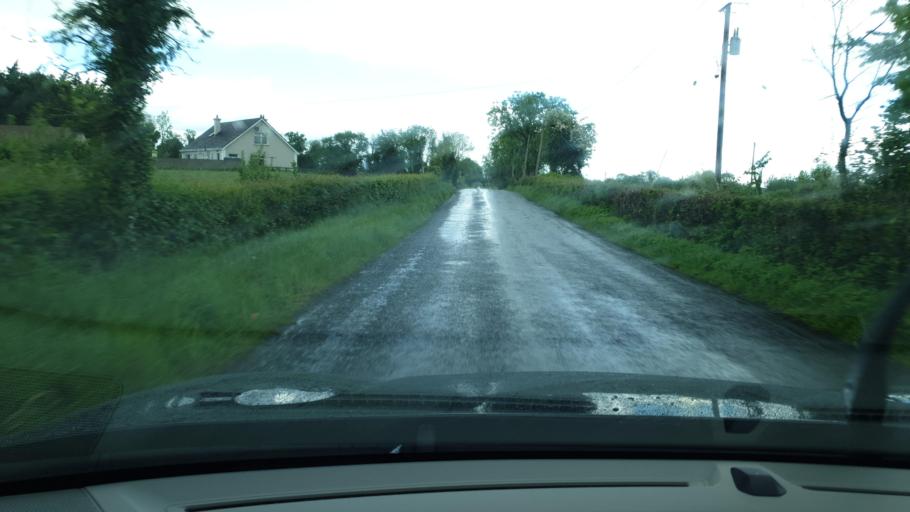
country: IE
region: Leinster
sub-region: Laois
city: Mountmellick
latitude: 53.1405
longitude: -7.3710
